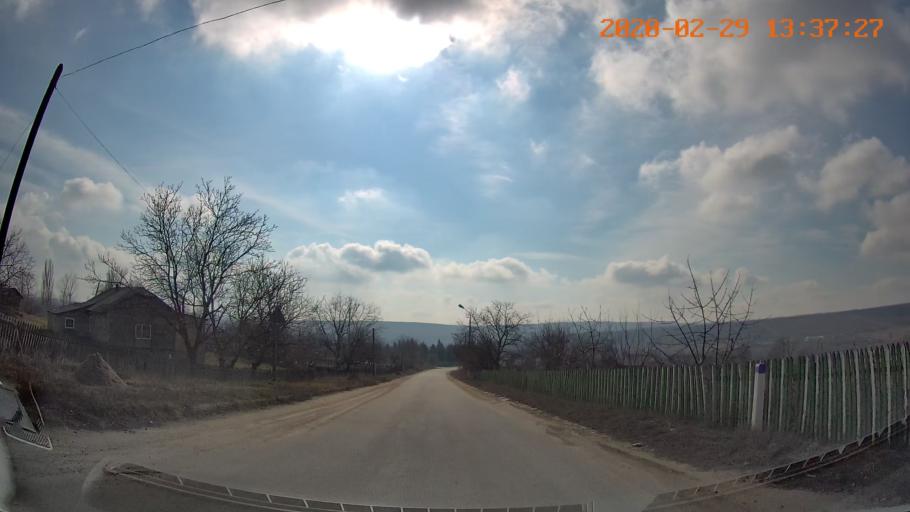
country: MD
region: Telenesti
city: Camenca
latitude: 47.8625
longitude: 28.6022
